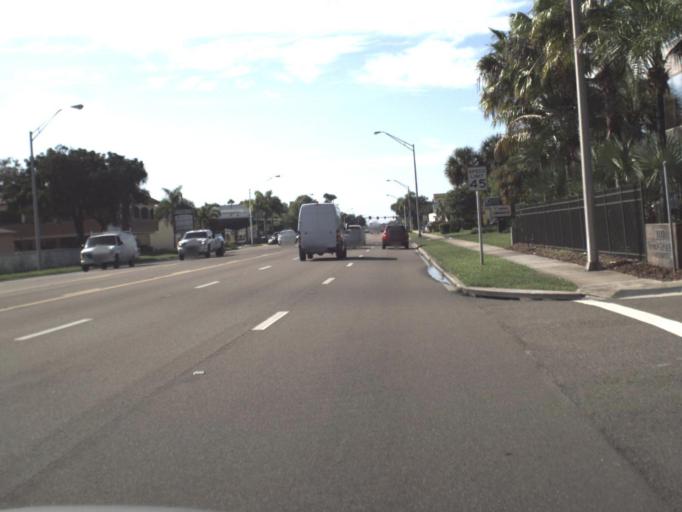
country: US
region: Florida
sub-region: Sarasota County
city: Southgate
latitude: 27.3068
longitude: -82.5302
